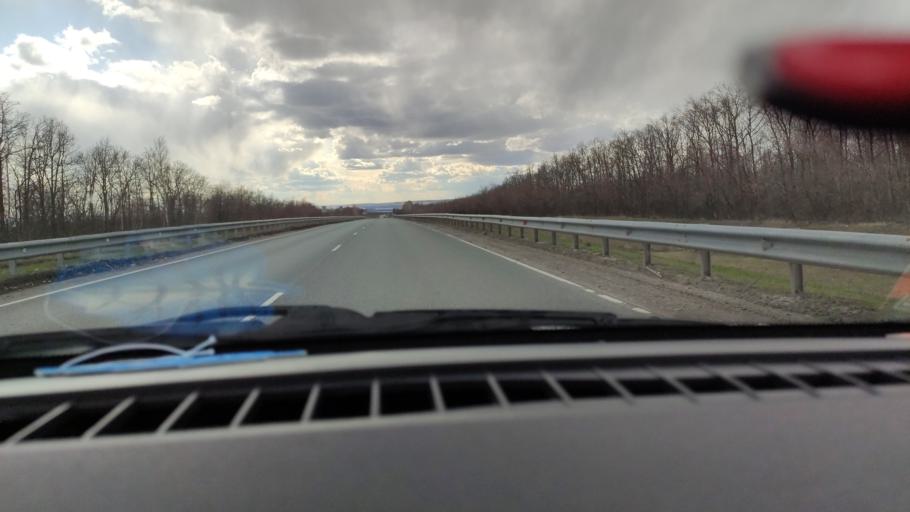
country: RU
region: Saratov
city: Balakovo
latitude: 52.0946
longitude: 47.7165
